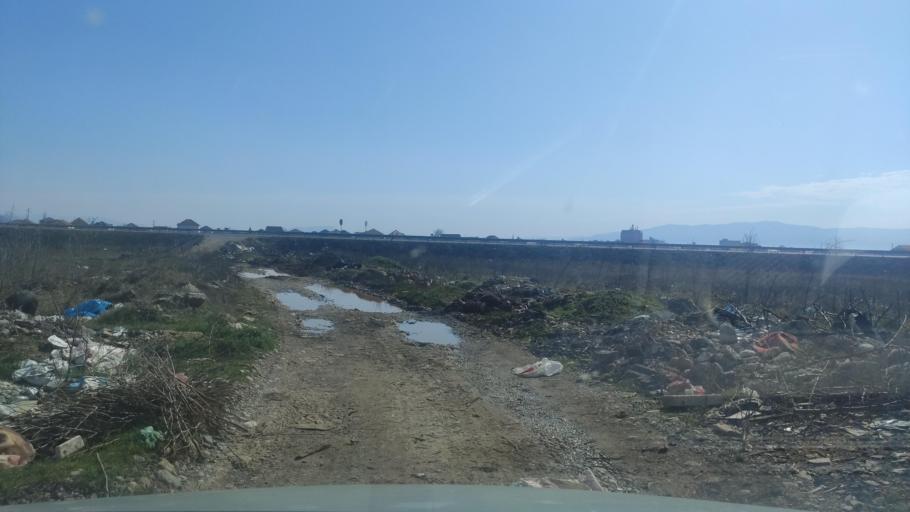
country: AL
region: Shkoder
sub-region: Rrethi i Malesia e Madhe
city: Koplik
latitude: 42.2228
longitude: 19.4352
